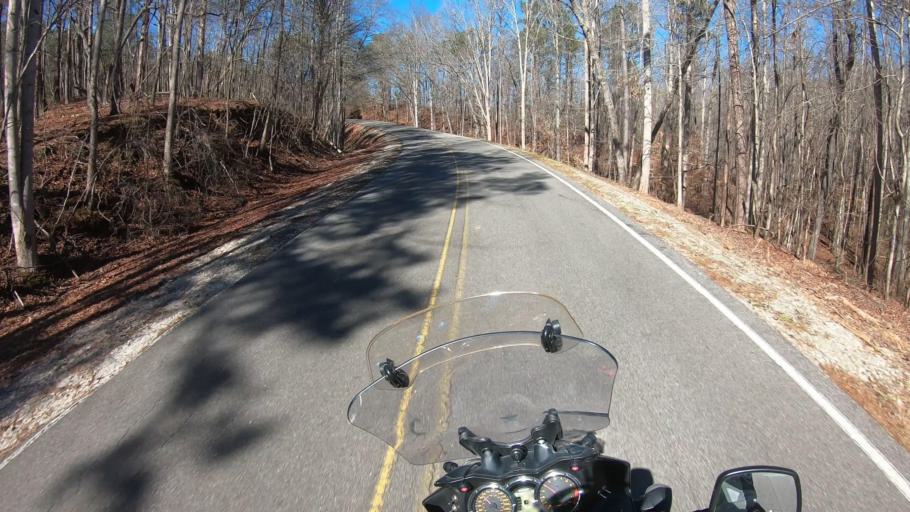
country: US
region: Alabama
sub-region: Clay County
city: Ashland
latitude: 33.3656
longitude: -85.8415
